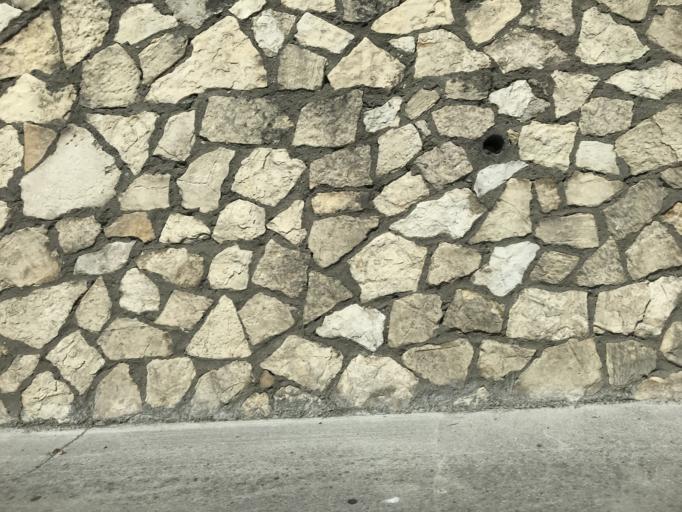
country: TR
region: Izmir
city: Izmir
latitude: 38.4135
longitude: 27.1564
